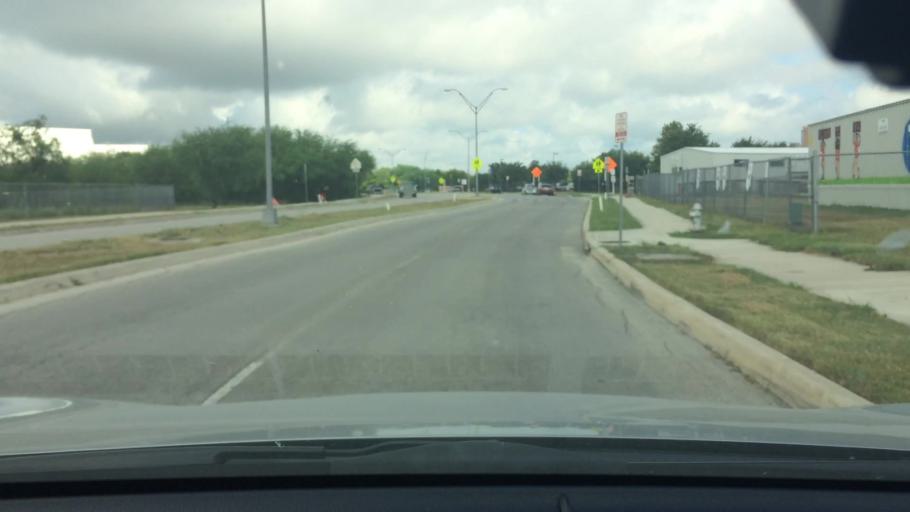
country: US
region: Texas
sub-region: Bexar County
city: China Grove
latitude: 29.3369
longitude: -98.4254
